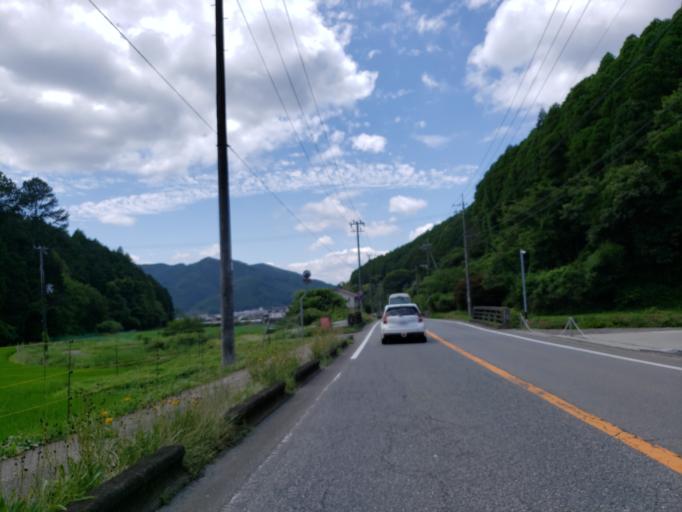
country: JP
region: Hyogo
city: Yamazakicho-nakabirose
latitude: 34.9859
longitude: 134.6089
